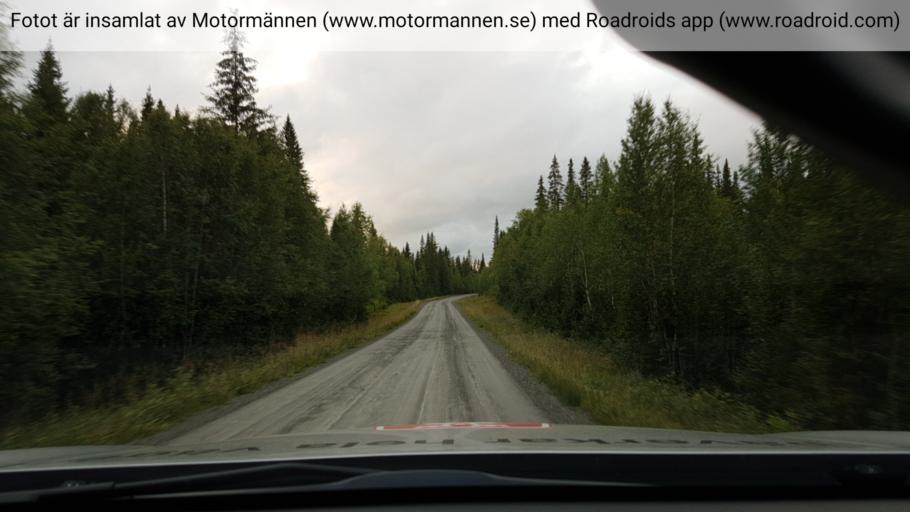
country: SE
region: Vaesterbotten
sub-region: Vilhelmina Kommun
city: Sjoberg
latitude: 65.5080
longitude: 15.4721
